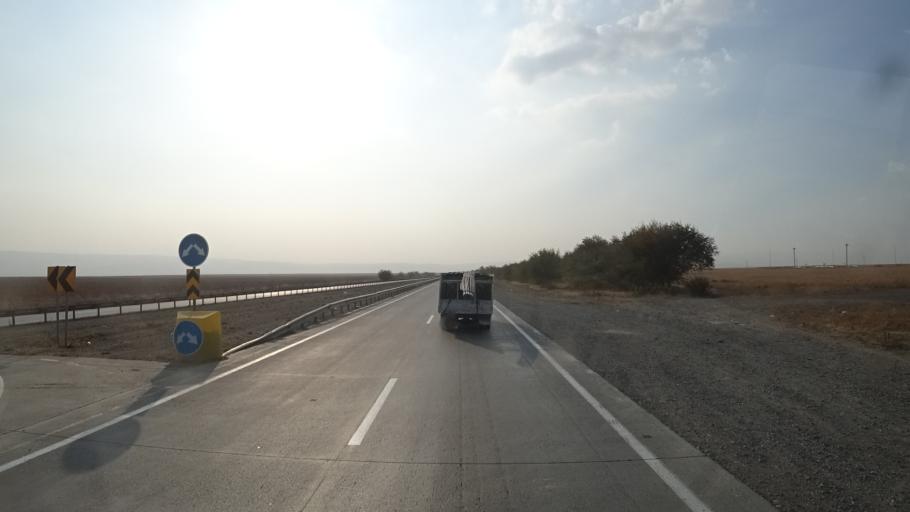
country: KZ
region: Zhambyl
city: Taraz
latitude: 42.8118
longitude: 71.1305
